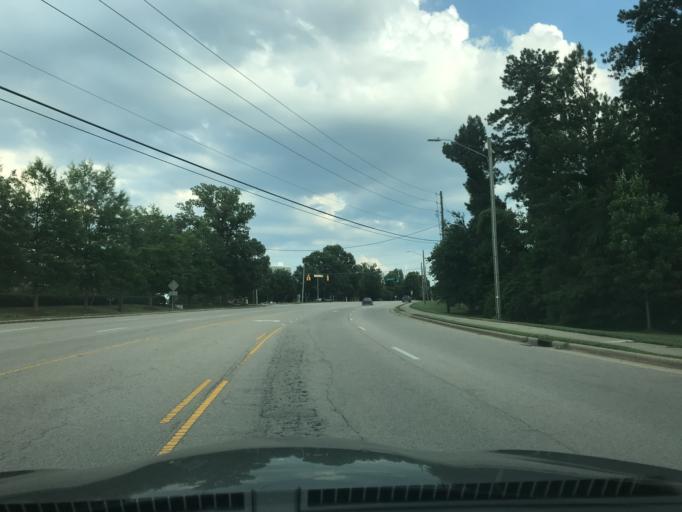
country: US
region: North Carolina
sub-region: Wake County
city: West Raleigh
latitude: 35.8223
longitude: -78.7055
